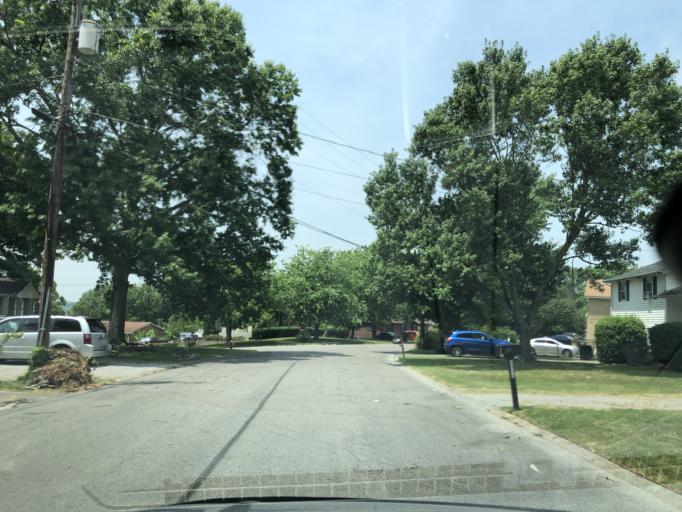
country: US
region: Tennessee
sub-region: Rutherford County
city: La Vergne
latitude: 36.0742
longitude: -86.6732
